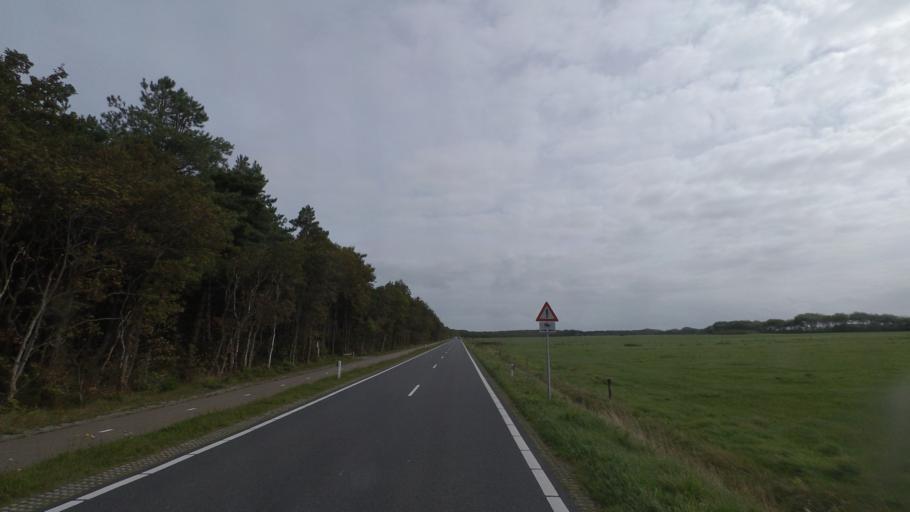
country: NL
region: Friesland
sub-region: Gemeente Ameland
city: Hollum
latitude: 53.4465
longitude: 5.7002
